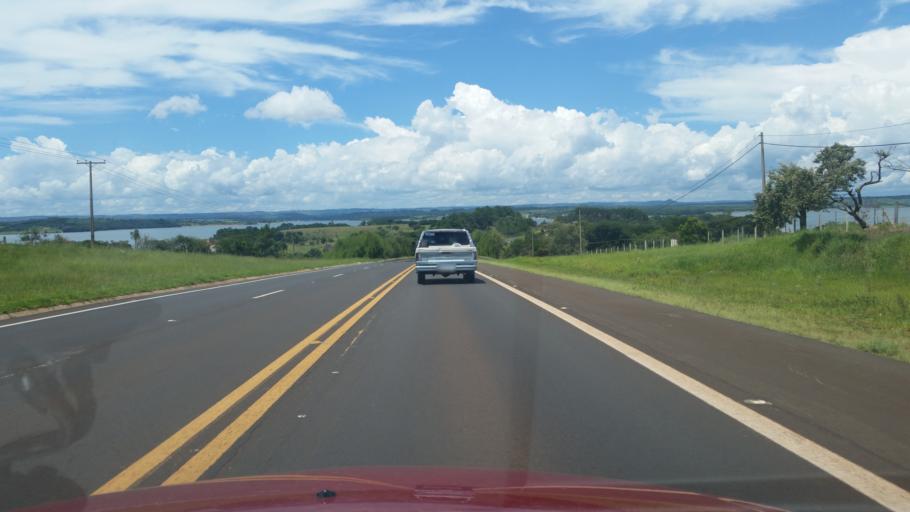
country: BR
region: Sao Paulo
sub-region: Itai
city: Itai
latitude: -23.2821
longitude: -49.0277
